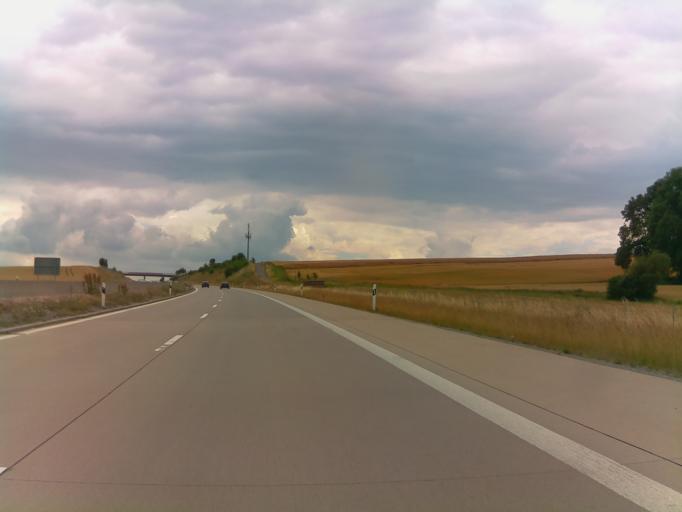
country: DE
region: Bavaria
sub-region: Regierungsbezirk Unterfranken
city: Hollstadt
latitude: 50.3791
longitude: 10.3126
